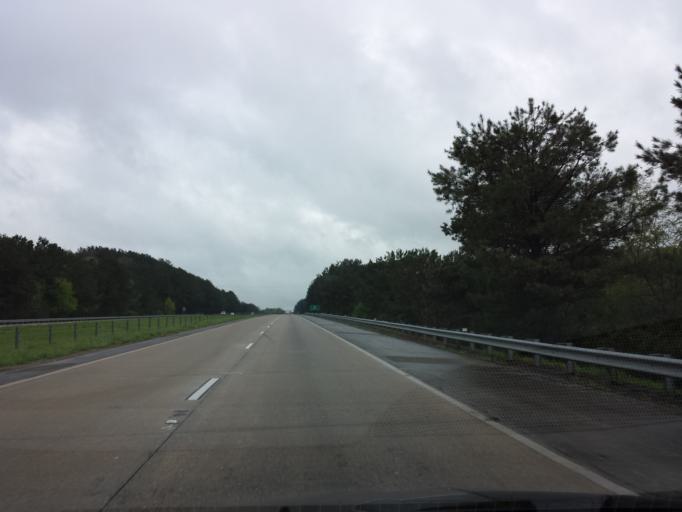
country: US
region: Georgia
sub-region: Cherokee County
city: Ball Ground
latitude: 34.3370
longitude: -84.3925
